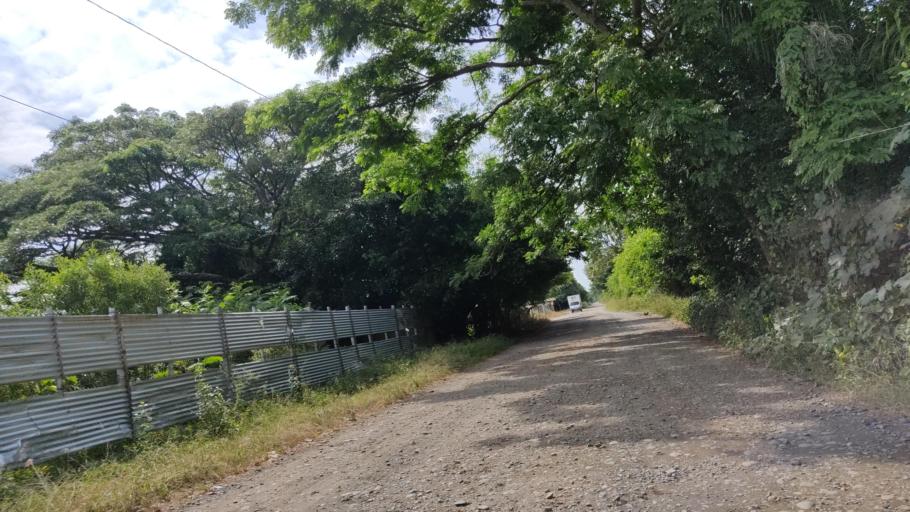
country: CO
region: Cauca
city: Buenos Aires
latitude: 3.1274
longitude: -76.5892
